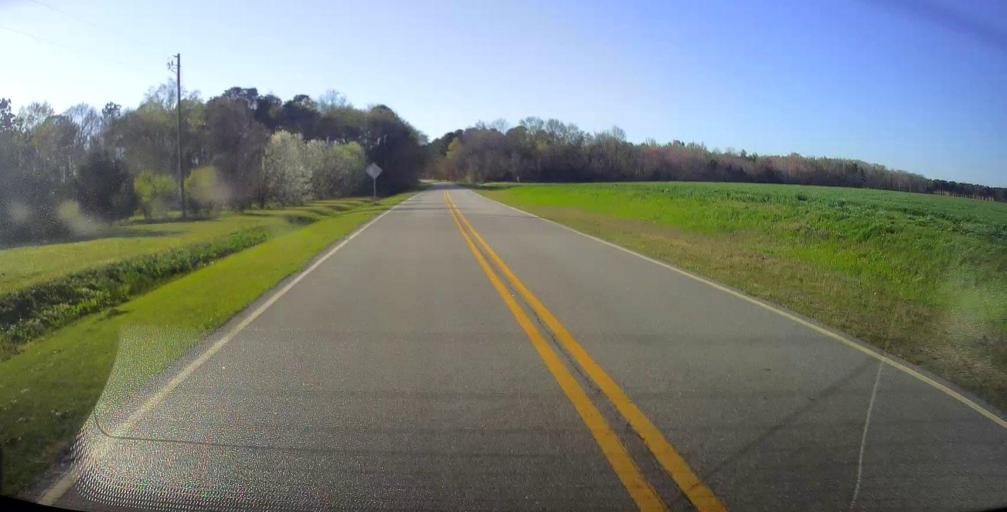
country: US
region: Georgia
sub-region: Houston County
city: Perry
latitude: 32.3584
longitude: -83.6424
